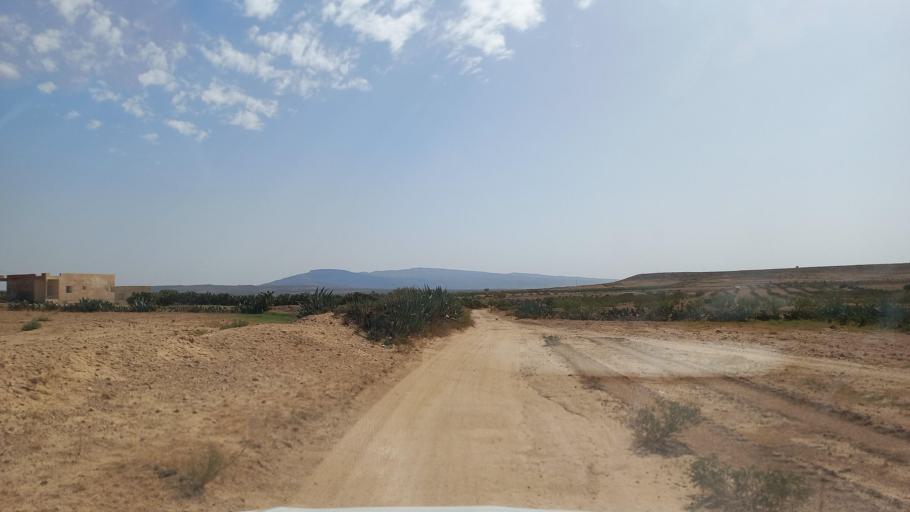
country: TN
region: Al Qasrayn
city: Kasserine
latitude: 35.2772
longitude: 8.9698
